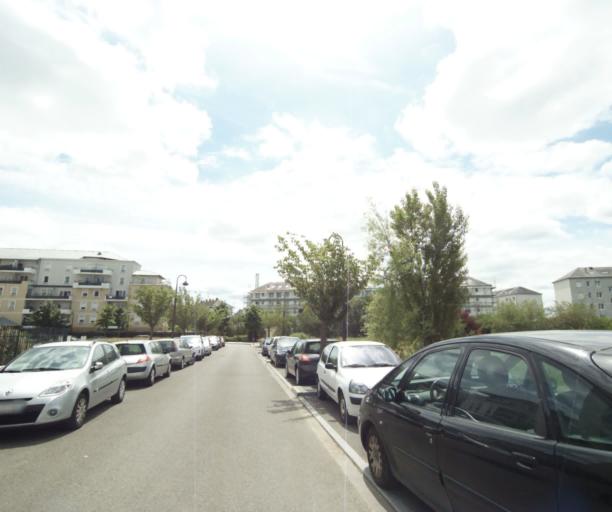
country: FR
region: Centre
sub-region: Departement d'Eure-et-Loir
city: Luce
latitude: 48.4395
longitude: 1.4711
